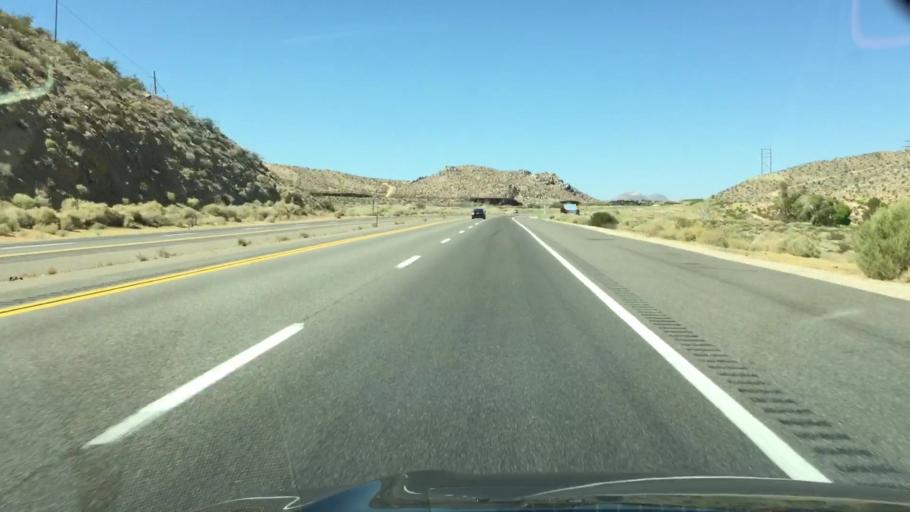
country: US
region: California
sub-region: Kern County
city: Inyokern
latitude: 35.9262
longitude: -117.9088
